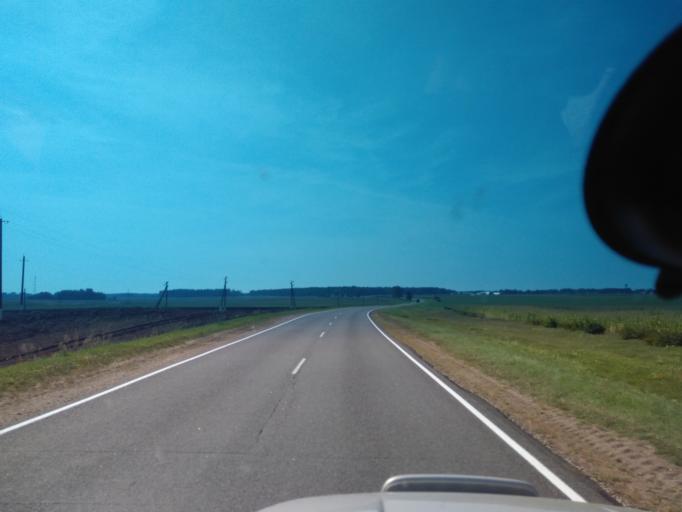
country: BY
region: Minsk
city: Uzda
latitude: 53.3683
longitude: 27.2317
